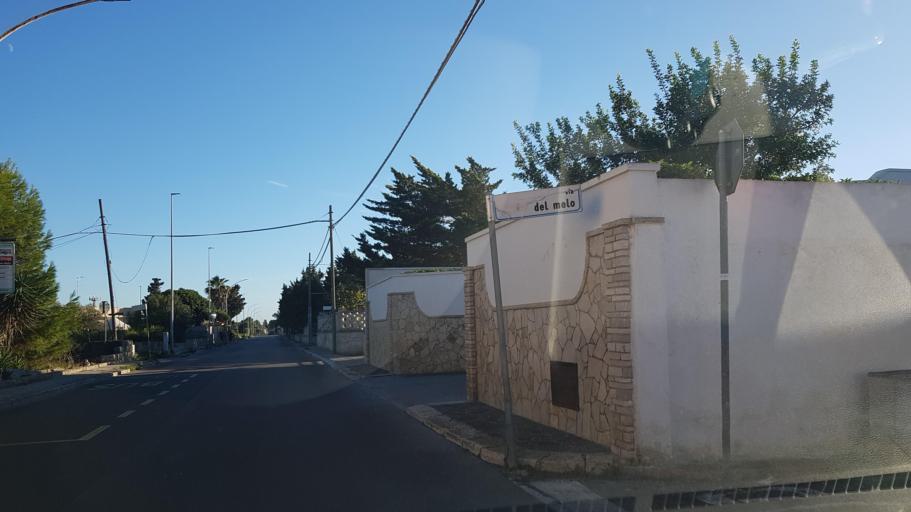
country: IT
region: Apulia
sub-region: Provincia di Lecce
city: Giorgilorio
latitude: 40.4634
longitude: 18.1951
